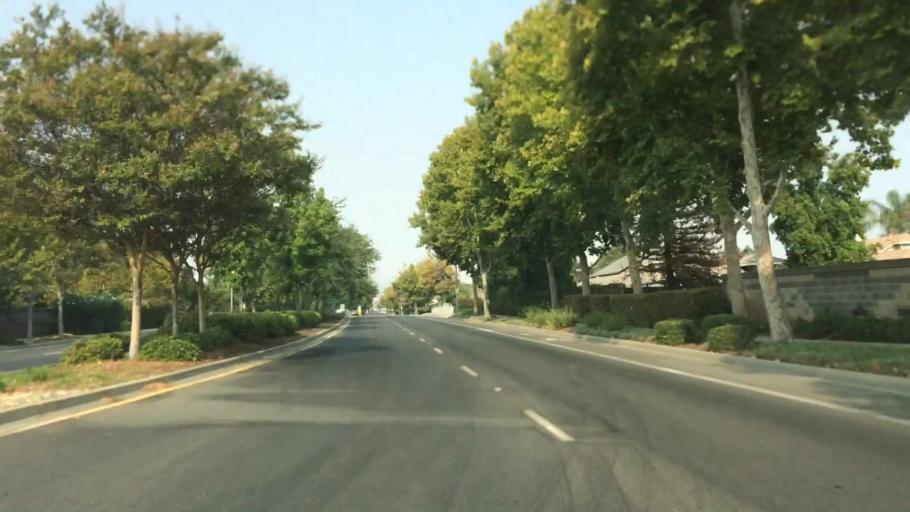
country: US
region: California
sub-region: Contra Costa County
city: Brentwood
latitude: 37.9255
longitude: -121.7088
